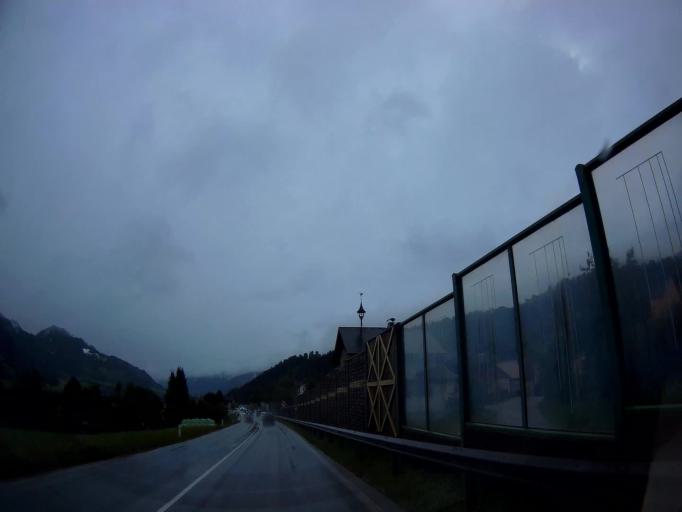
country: AT
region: Styria
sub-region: Politischer Bezirk Liezen
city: Haus im Ennstal
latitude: 47.4134
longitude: 13.7843
